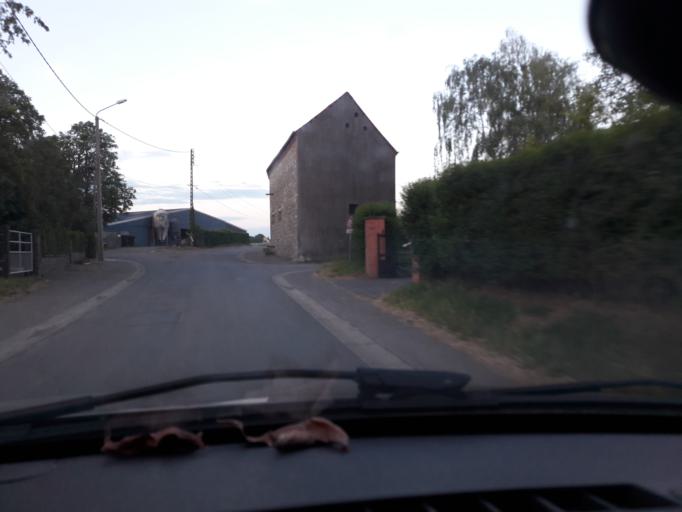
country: BE
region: Wallonia
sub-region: Province du Hainaut
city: Beaumont
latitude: 50.2641
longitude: 4.1861
